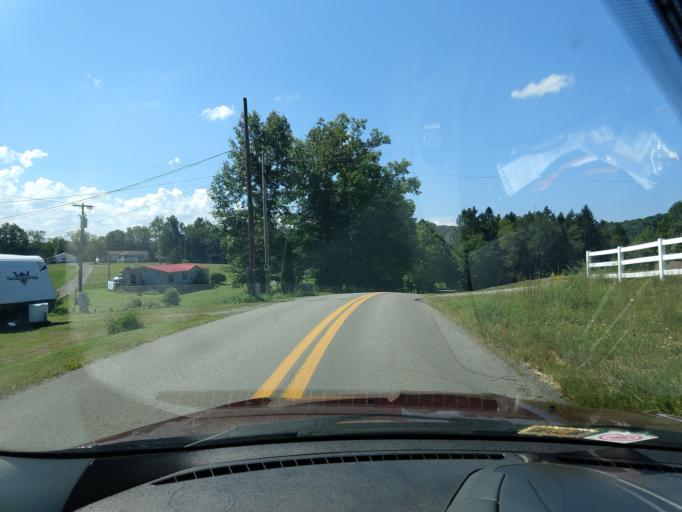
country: US
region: West Virginia
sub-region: Nicholas County
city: Summersville
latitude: 38.2728
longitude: -80.7726
